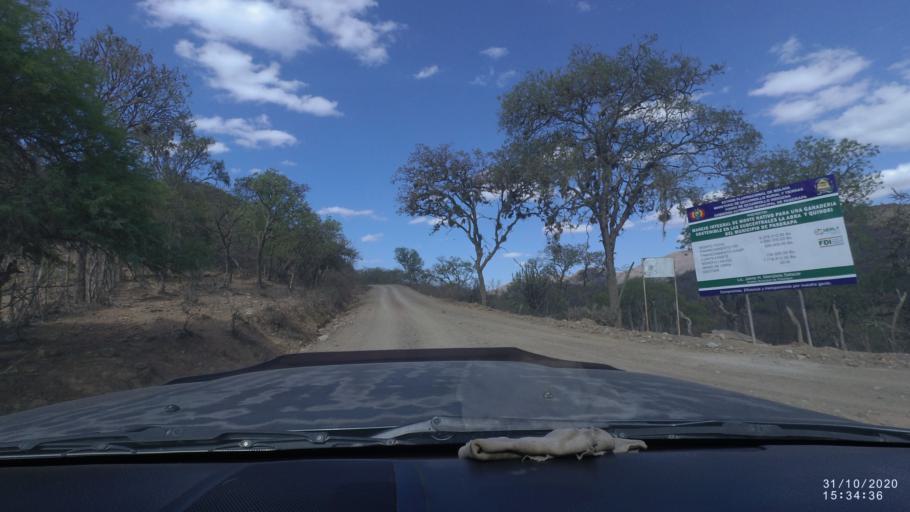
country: BO
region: Chuquisaca
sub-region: Provincia Zudanez
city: Mojocoya
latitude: -18.3421
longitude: -64.7533
